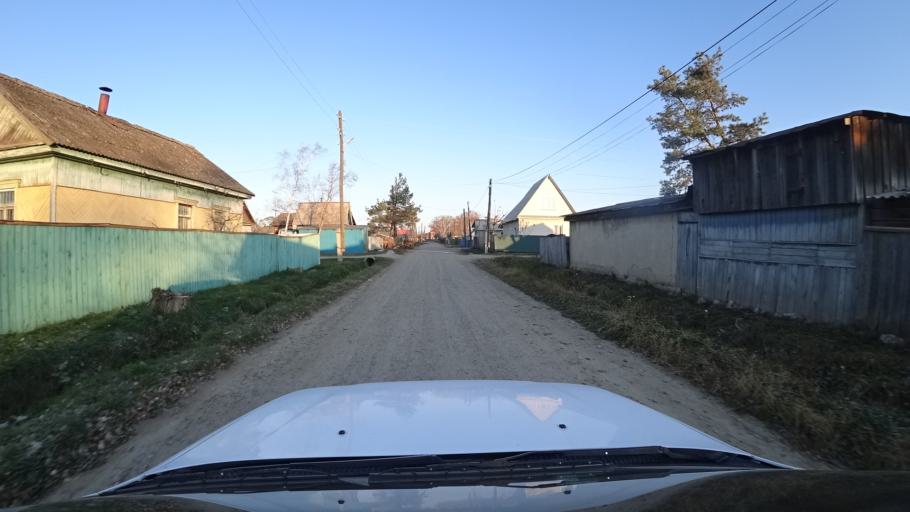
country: RU
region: Primorskiy
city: Dal'nerechensk
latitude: 45.9237
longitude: 133.7229
